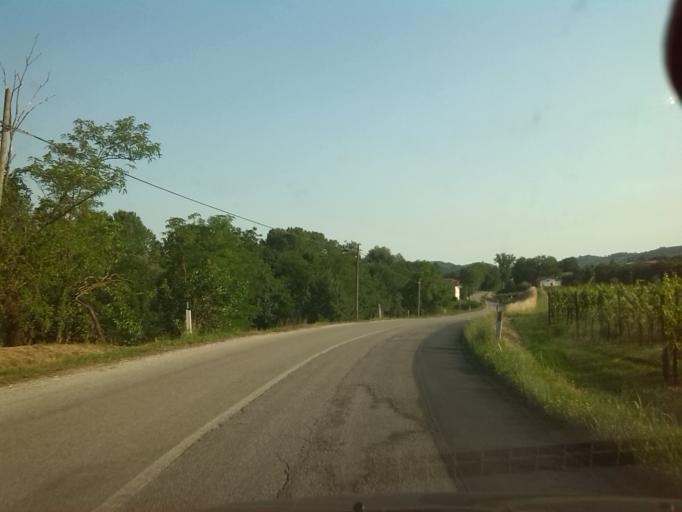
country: IT
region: Friuli Venezia Giulia
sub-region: Provincia di Gorizia
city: Dolegna del Collio
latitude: 46.0368
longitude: 13.4779
